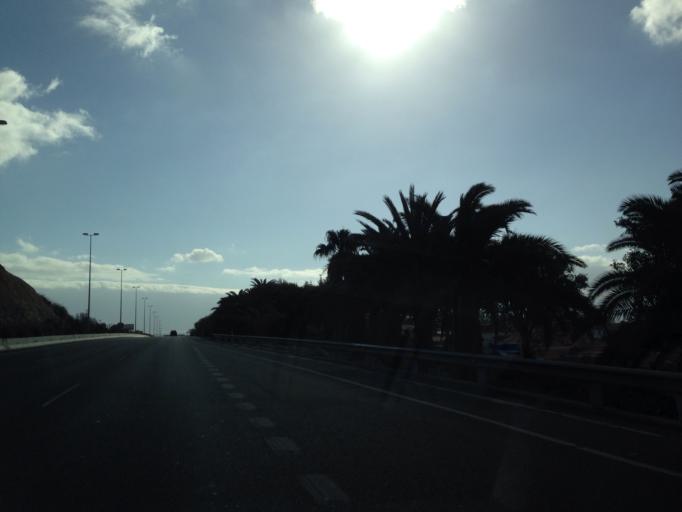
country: ES
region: Canary Islands
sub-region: Provincia de Las Palmas
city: Maspalomas
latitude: 27.7715
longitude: -15.5767
